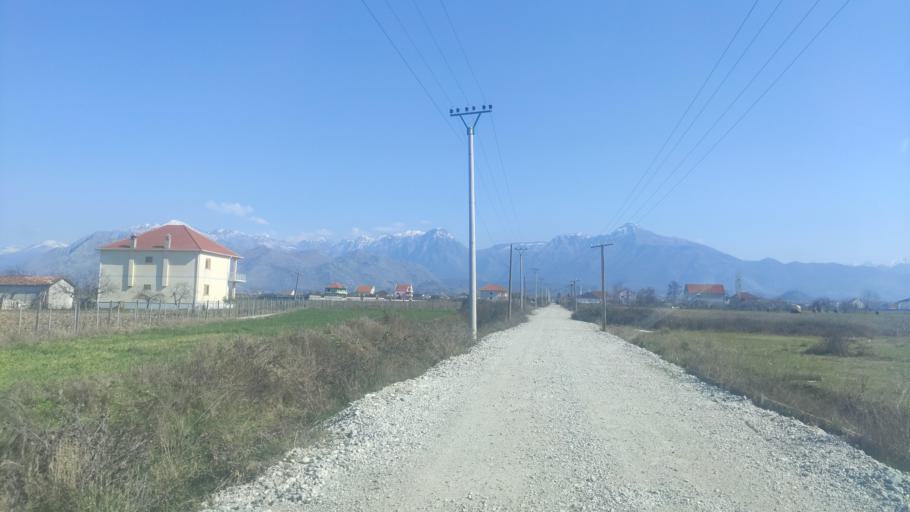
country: AL
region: Shkoder
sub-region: Rrethi i Malesia e Madhe
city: Grude-Fushe
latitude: 42.1593
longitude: 19.4510
